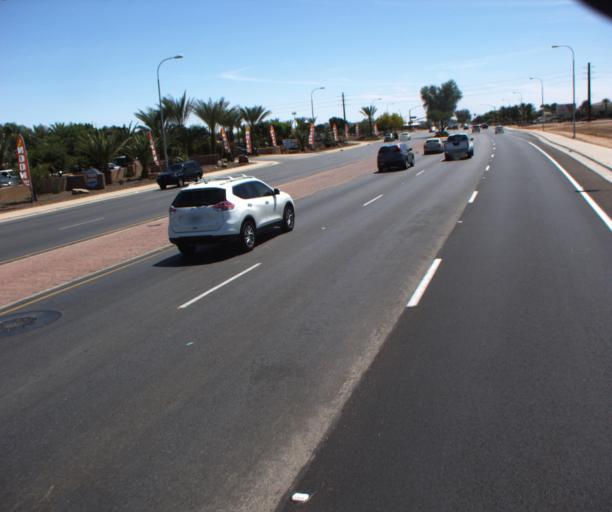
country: US
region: Arizona
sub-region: Maricopa County
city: Chandler
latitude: 33.2792
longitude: -111.8417
